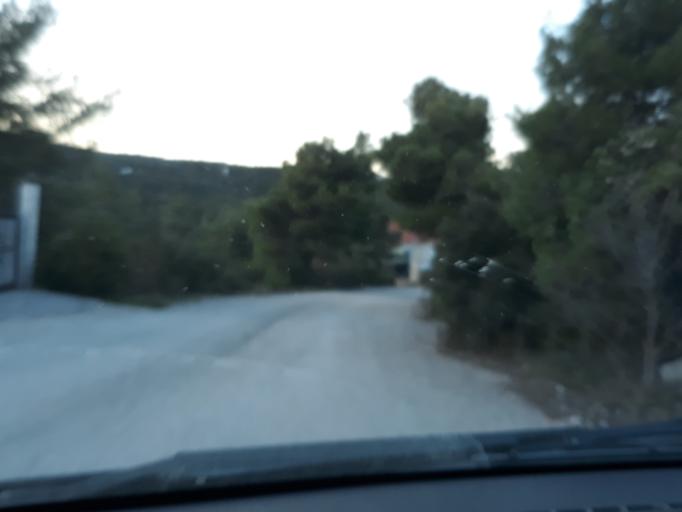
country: GR
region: Attica
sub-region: Nomarchia Anatolikis Attikis
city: Afidnes
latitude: 38.1951
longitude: 23.7957
